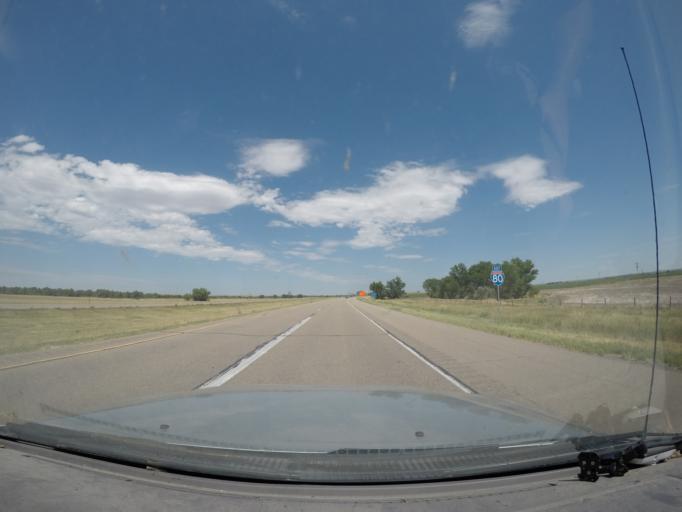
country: US
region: Colorado
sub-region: Sedgwick County
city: Julesburg
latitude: 41.0345
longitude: -102.1405
